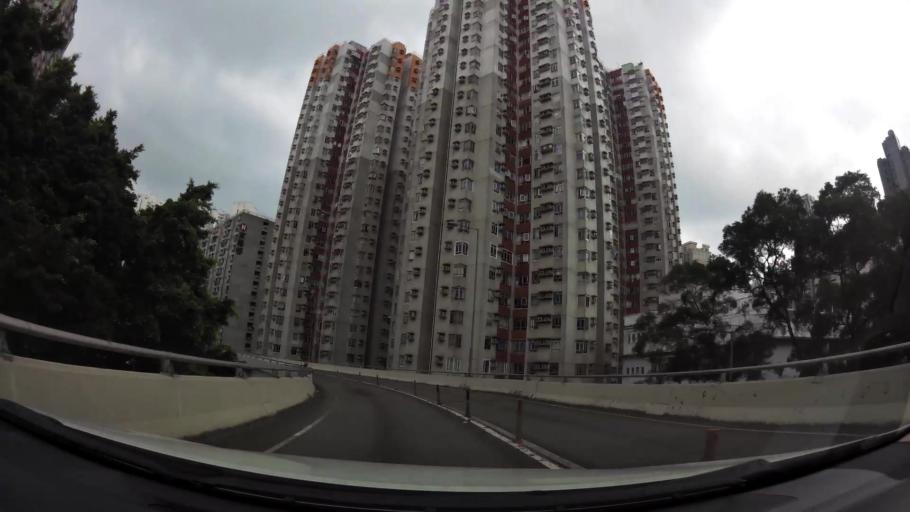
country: HK
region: Kowloon City
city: Kowloon
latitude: 22.3091
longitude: 114.1859
